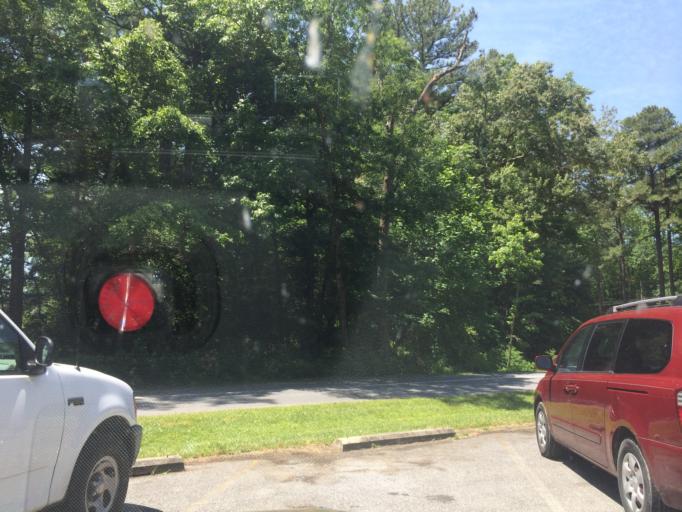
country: US
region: Delaware
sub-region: Sussex County
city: Laurel
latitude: 38.5302
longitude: -75.4801
